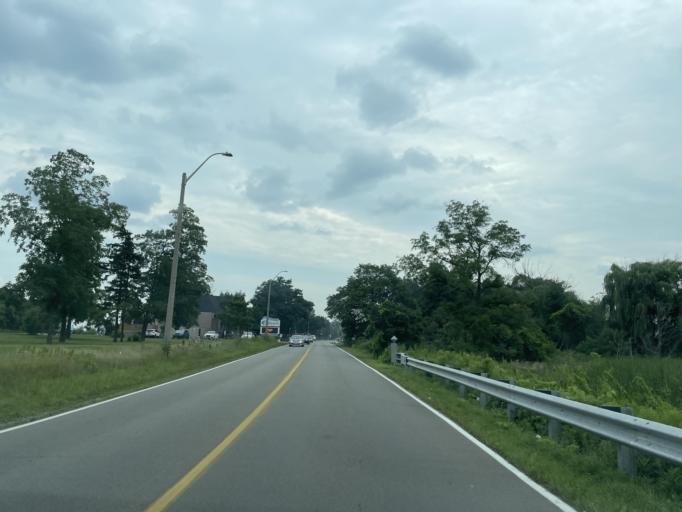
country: CA
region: Ontario
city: Hamilton
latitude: 43.2563
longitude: -79.7631
